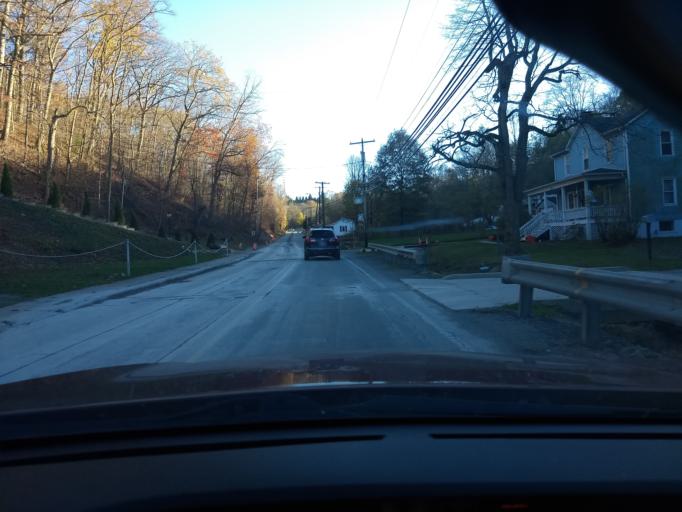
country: US
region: Pennsylvania
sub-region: Allegheny County
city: Oakdale
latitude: 40.3953
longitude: -80.1844
